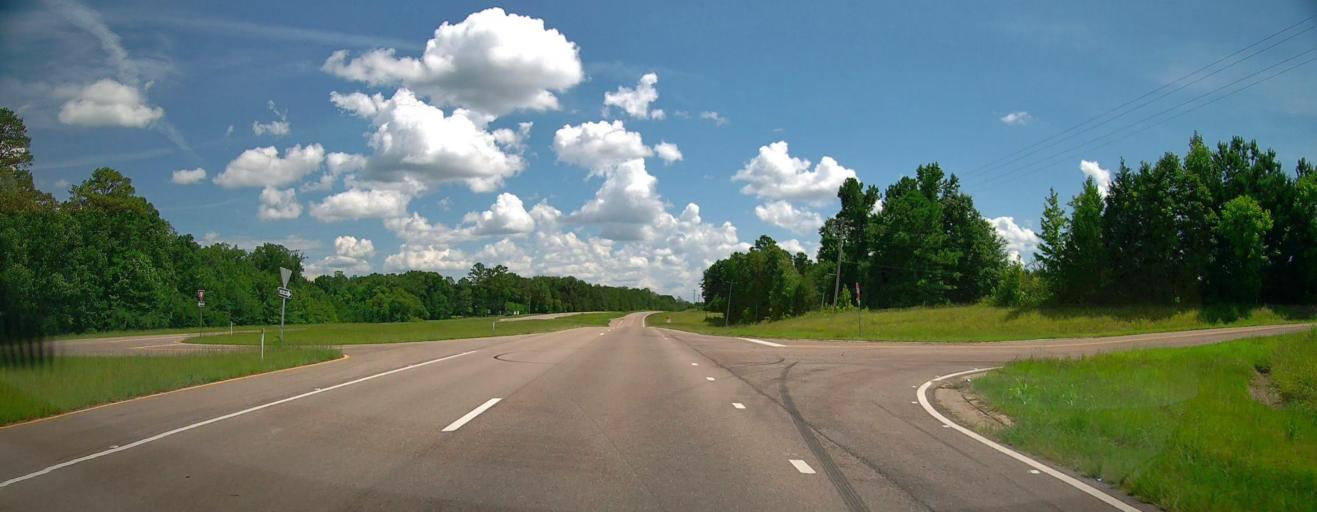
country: US
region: Mississippi
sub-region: Monroe County
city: Amory
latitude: 33.9430
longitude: -88.5996
